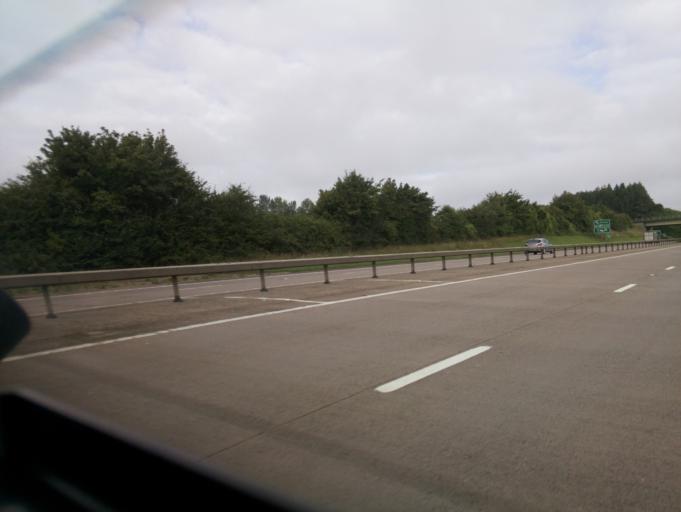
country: GB
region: England
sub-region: Gloucestershire
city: Cirencester
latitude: 51.7179
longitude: -1.9394
